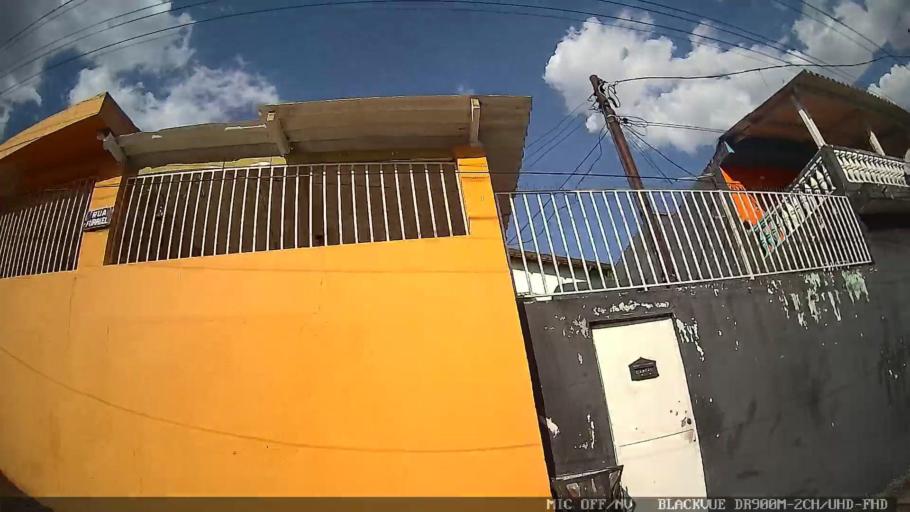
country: BR
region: Sao Paulo
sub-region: Ferraz De Vasconcelos
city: Ferraz de Vasconcelos
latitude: -23.5200
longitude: -46.4249
